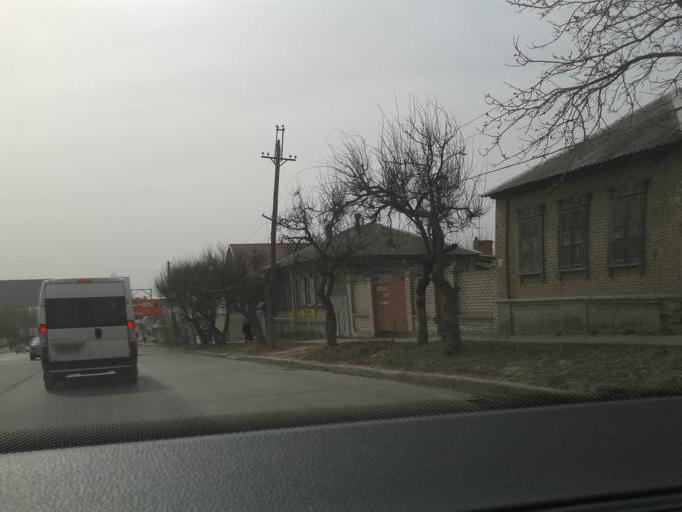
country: RU
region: Volgograd
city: Volgograd
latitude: 48.7176
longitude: 44.5036
